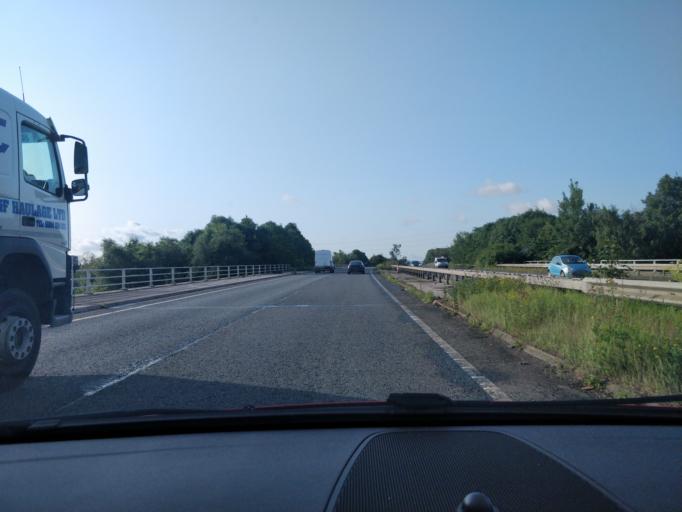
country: GB
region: England
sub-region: Knowsley
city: Whiston
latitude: 53.4000
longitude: -2.8096
